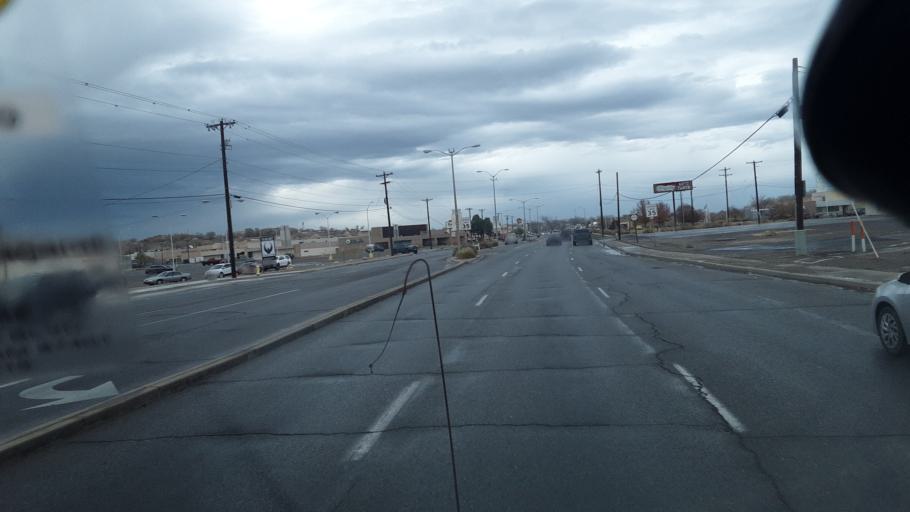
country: US
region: New Mexico
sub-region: San Juan County
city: Farmington
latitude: 36.7432
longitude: -108.1672
